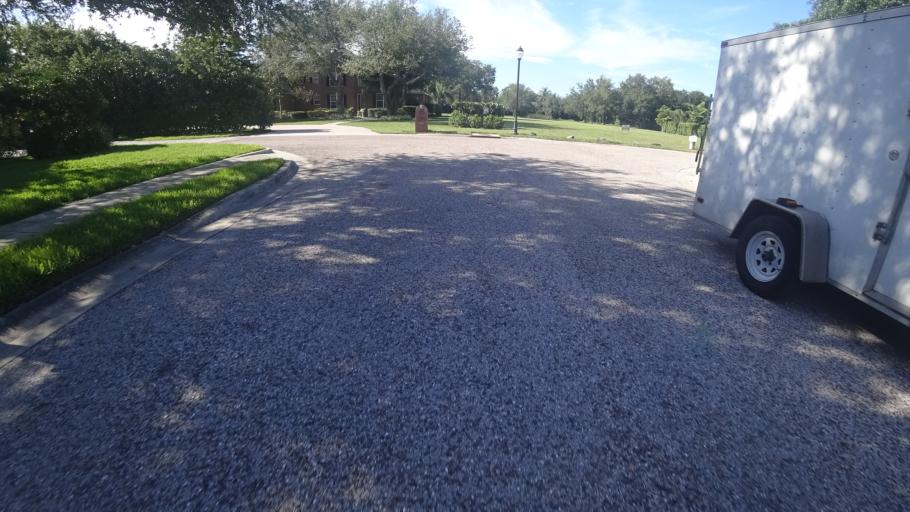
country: US
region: Florida
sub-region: Manatee County
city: West Bradenton
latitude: 27.5123
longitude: -82.6503
